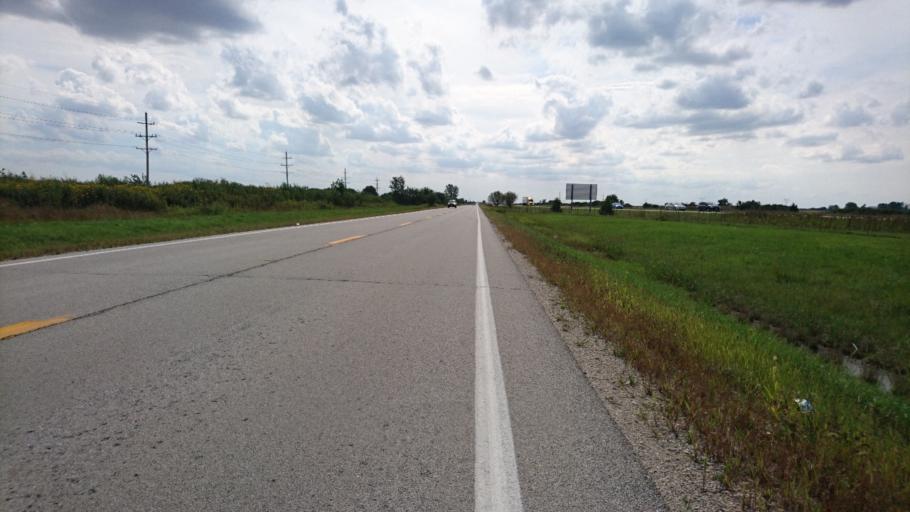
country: US
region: Illinois
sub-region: Grundy County
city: Gardner
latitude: 41.1746
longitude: -88.3254
